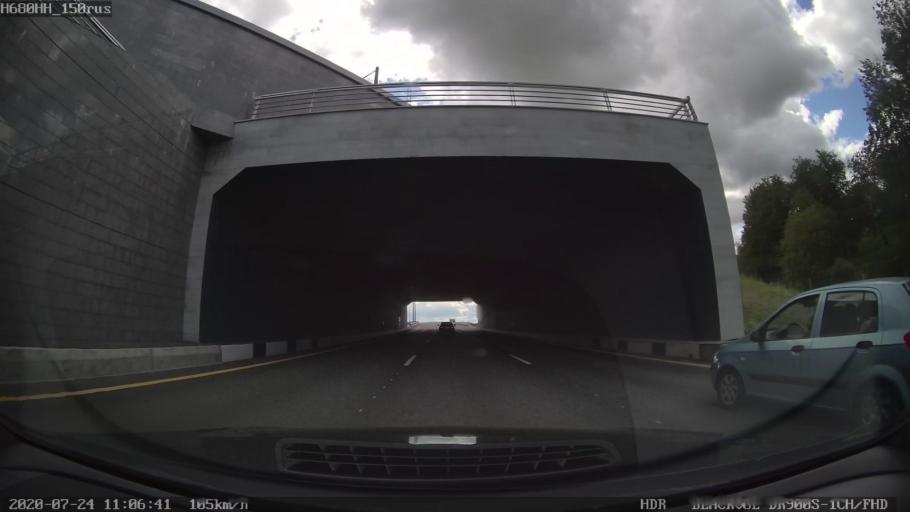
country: RU
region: St.-Petersburg
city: Pushkin
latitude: 59.7605
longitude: 30.3817
